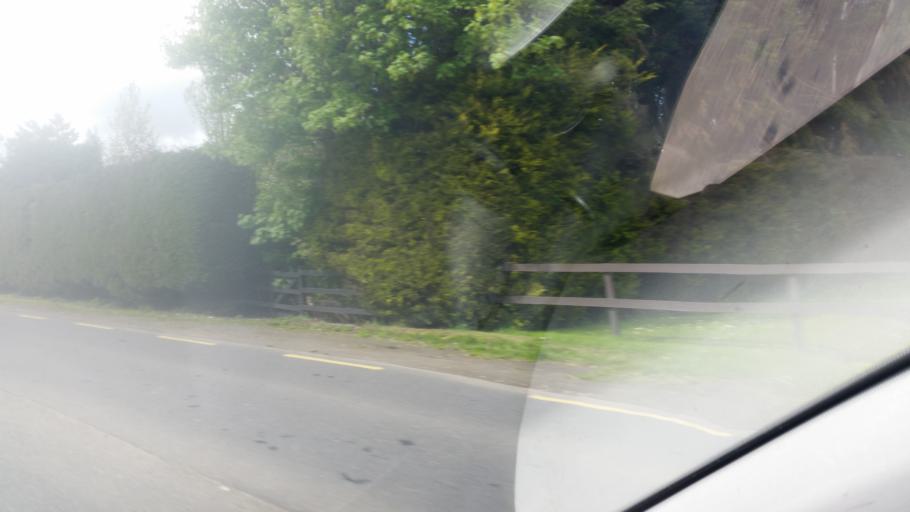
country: IE
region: Leinster
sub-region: Loch Garman
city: Loch Garman
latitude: 52.3492
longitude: -6.4558
